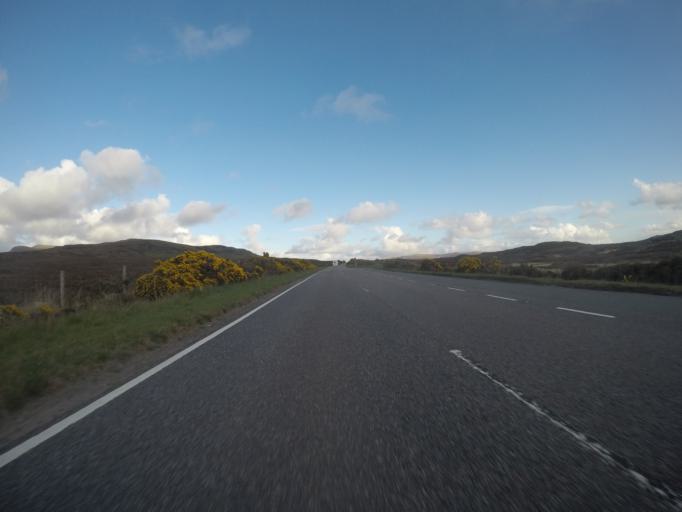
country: GB
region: Scotland
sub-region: Highland
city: Portree
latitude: 57.4725
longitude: -6.2954
